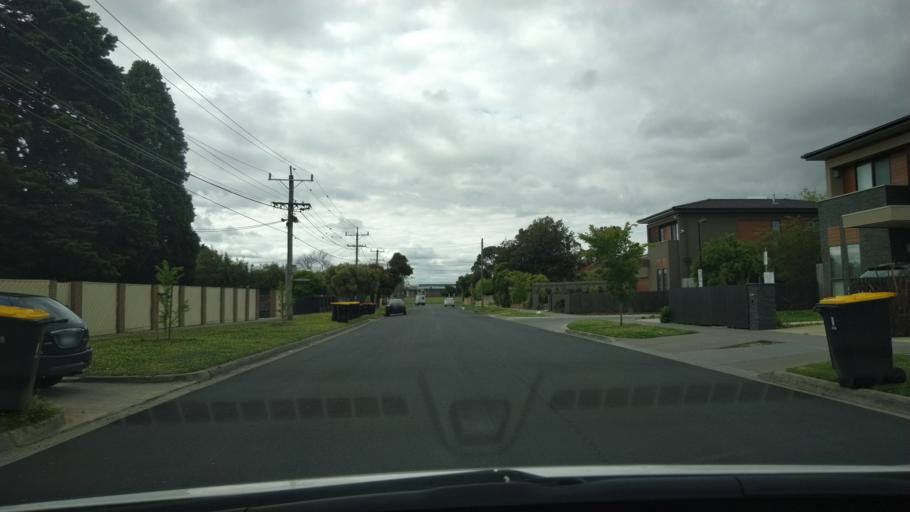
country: AU
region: Victoria
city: Highett
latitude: -37.9557
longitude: 145.0668
